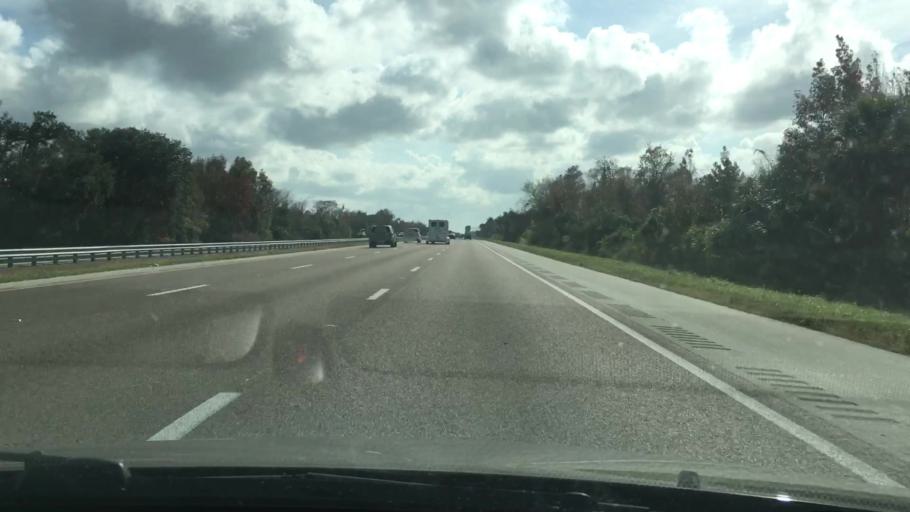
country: US
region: Florida
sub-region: Volusia County
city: Oak Hill
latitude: 28.7962
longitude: -80.9011
